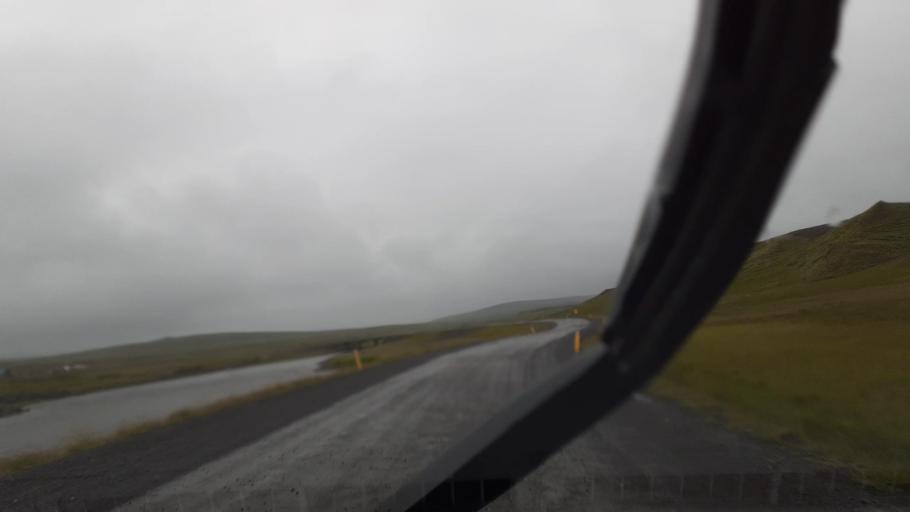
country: IS
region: East
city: Egilsstadir
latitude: 66.0432
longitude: -15.0962
